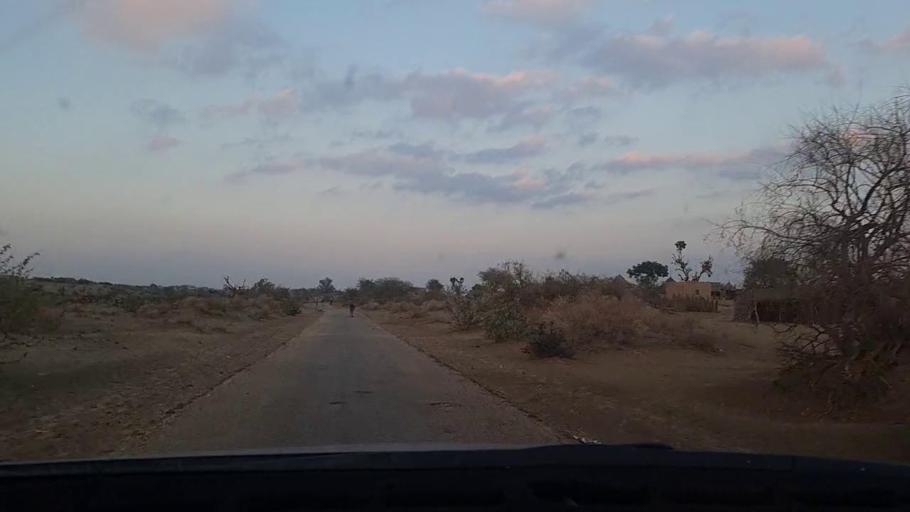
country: PK
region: Sindh
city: Tando Mittha Khan
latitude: 25.9609
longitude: 69.3443
